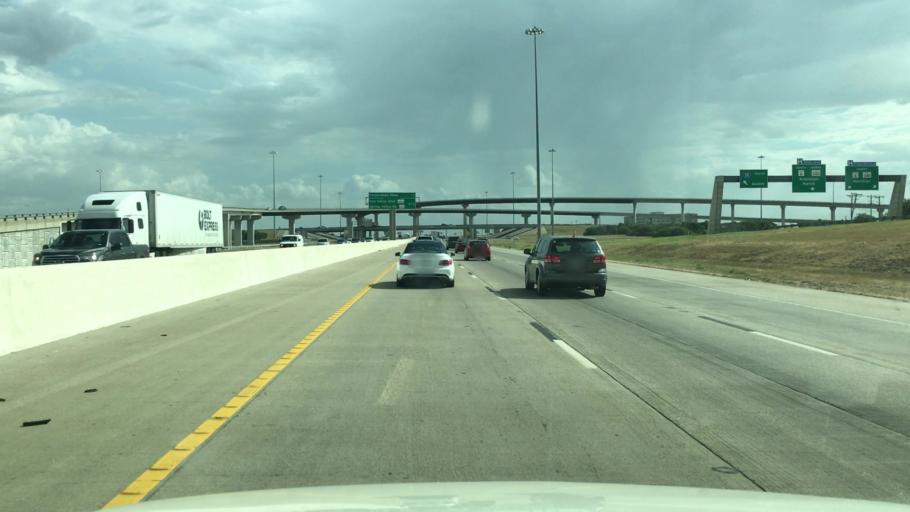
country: US
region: Texas
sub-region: McLennan County
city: Beverly Hills
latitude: 31.4981
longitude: -97.1482
